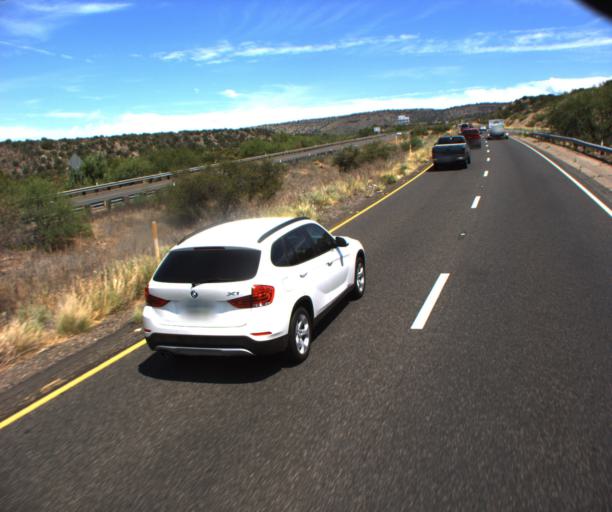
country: US
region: Arizona
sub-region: Yavapai County
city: Lake Montezuma
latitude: 34.6908
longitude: -111.7432
